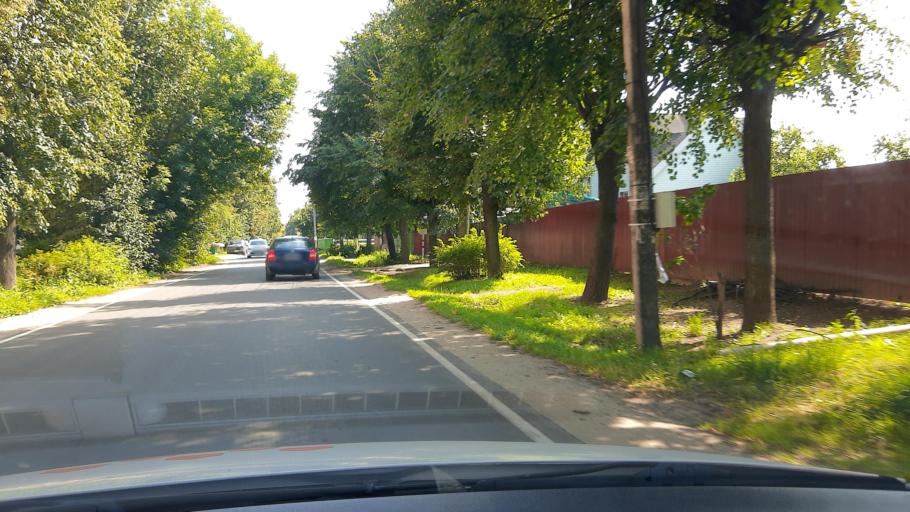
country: RU
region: Moskovskaya
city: Bronnitsy
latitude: 55.4227
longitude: 38.2633
